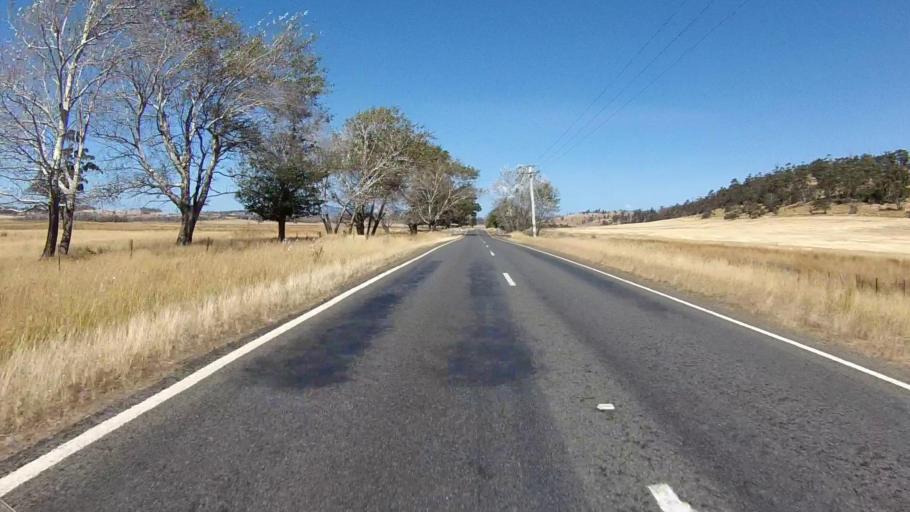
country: AU
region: Tasmania
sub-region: Sorell
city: Sorell
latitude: -42.4730
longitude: 147.9265
